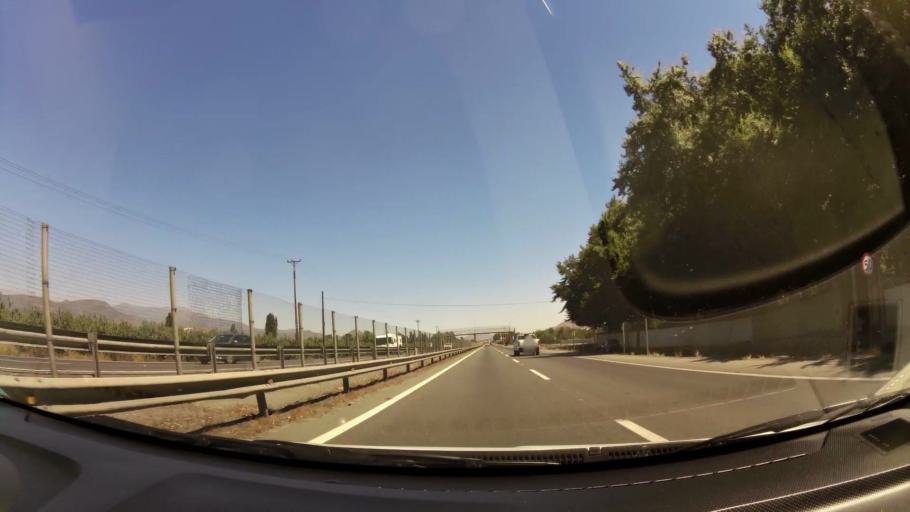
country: CL
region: O'Higgins
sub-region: Provincia de Cachapoal
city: Rengo
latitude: -34.3837
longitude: -70.8623
